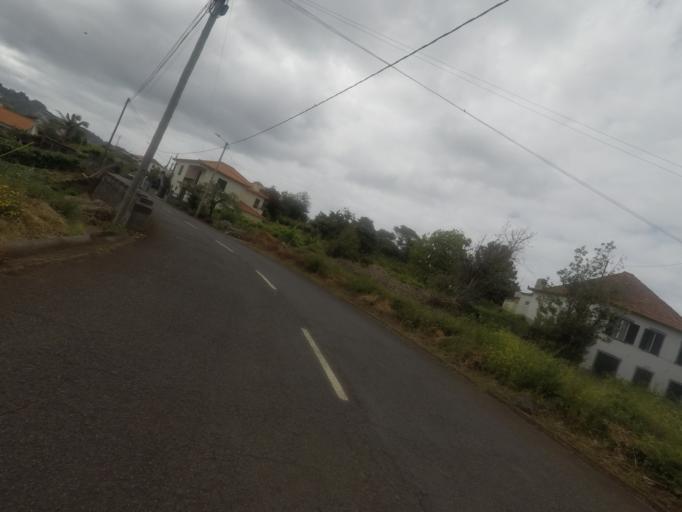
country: PT
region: Madeira
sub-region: Santana
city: Santana
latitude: 32.8235
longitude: -16.8867
